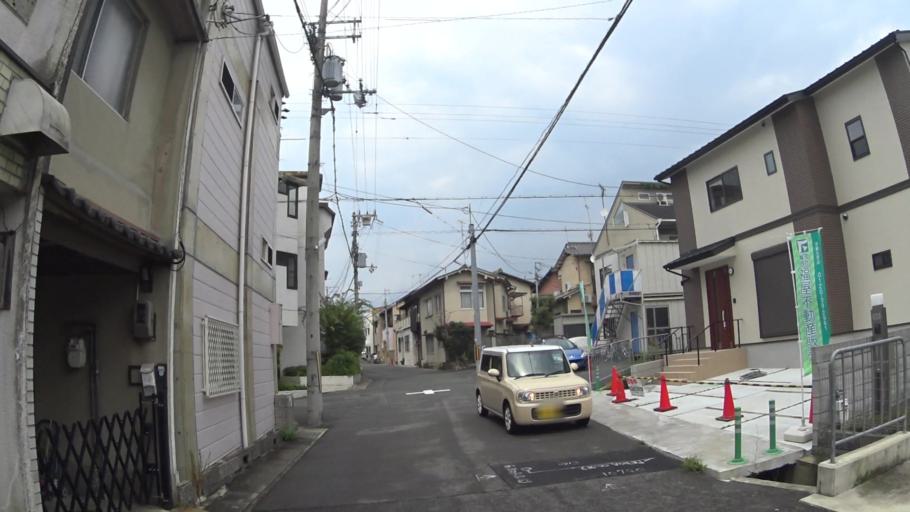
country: JP
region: Kyoto
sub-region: Kyoto-shi
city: Kamigyo-ku
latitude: 35.0409
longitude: 135.7934
